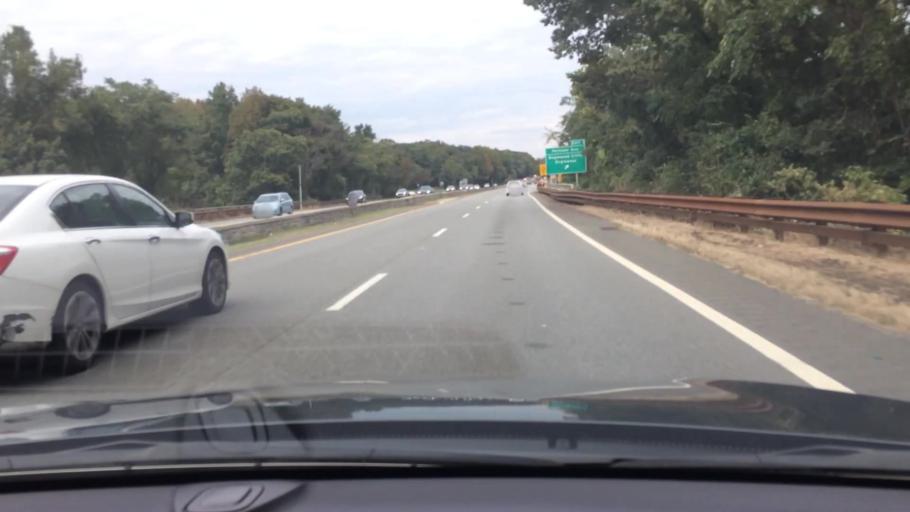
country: US
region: New Jersey
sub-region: Bergen County
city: Englewood Cliffs
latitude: 40.8785
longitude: -73.9494
